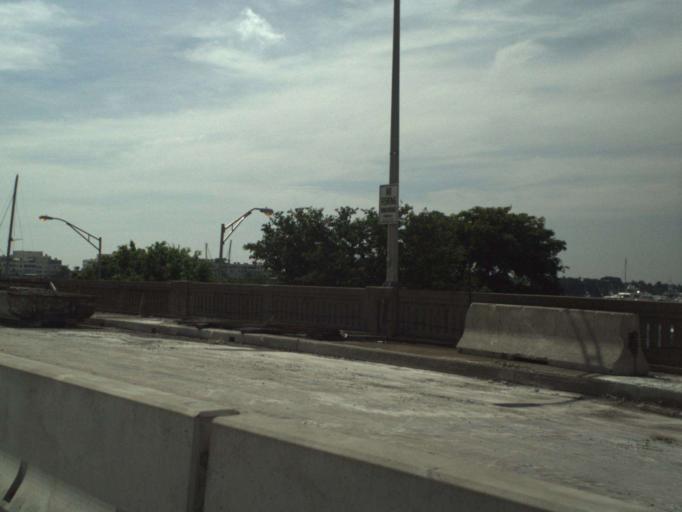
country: US
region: Florida
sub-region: Palm Beach County
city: West Palm Beach
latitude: 26.7184
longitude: -80.0504
